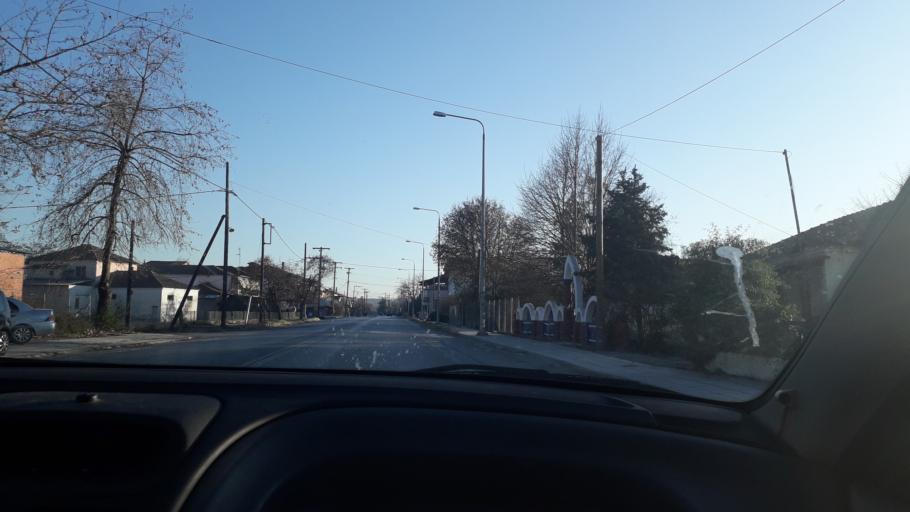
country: GR
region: Central Macedonia
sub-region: Nomos Imathias
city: Alexandreia
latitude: 40.5956
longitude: 22.4635
